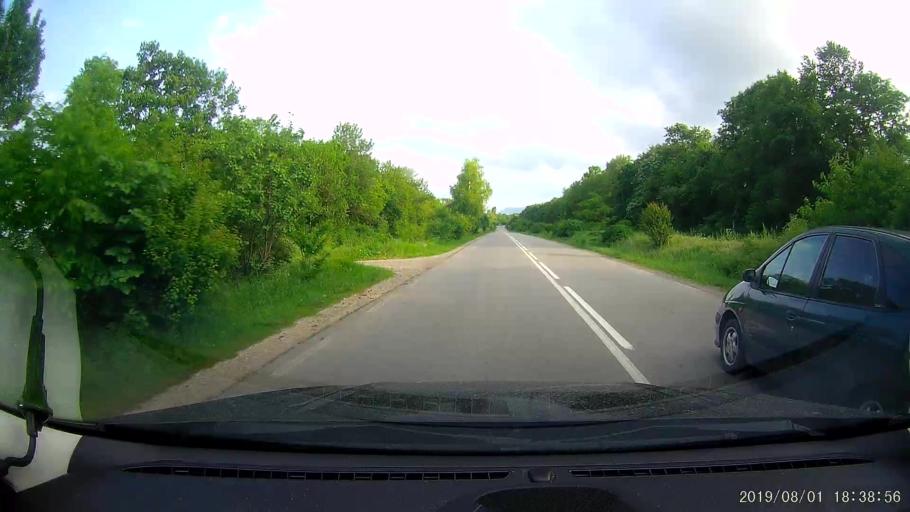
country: BG
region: Shumen
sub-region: Obshtina Khitrino
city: Gara Khitrino
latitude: 43.3956
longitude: 26.9172
